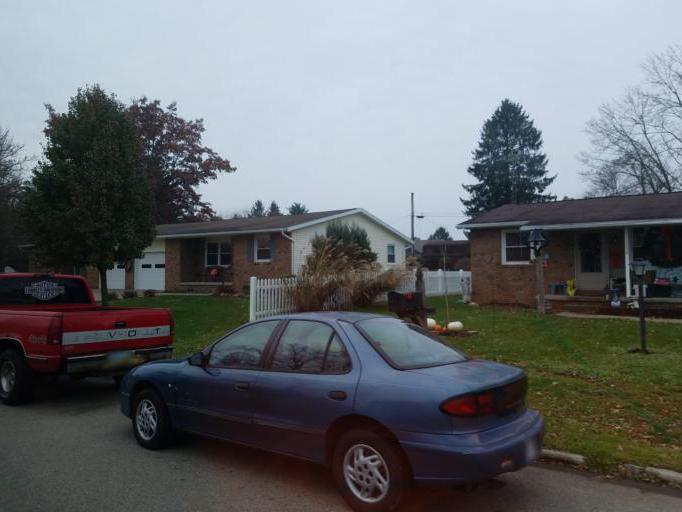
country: US
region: Ohio
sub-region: Richland County
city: Mansfield
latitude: 40.7216
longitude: -82.5321
